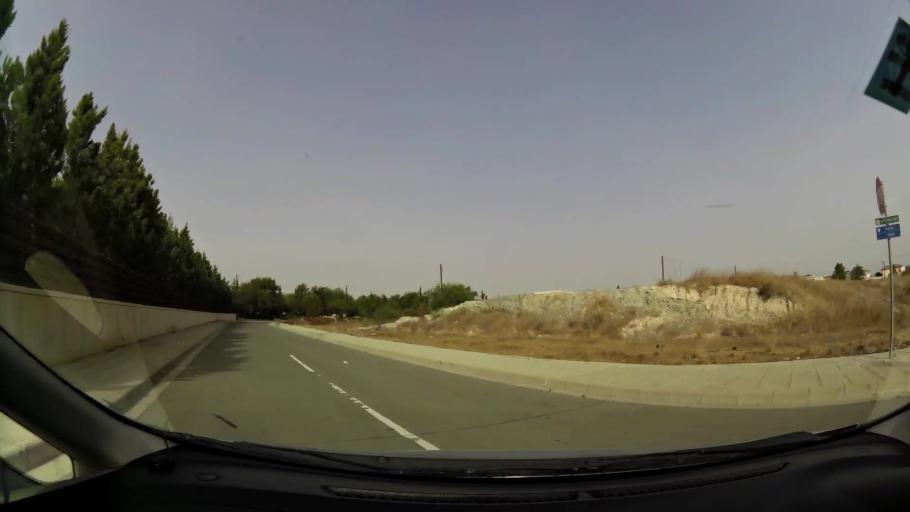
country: CY
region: Lefkosia
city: Geri
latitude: 35.0786
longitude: 33.3888
